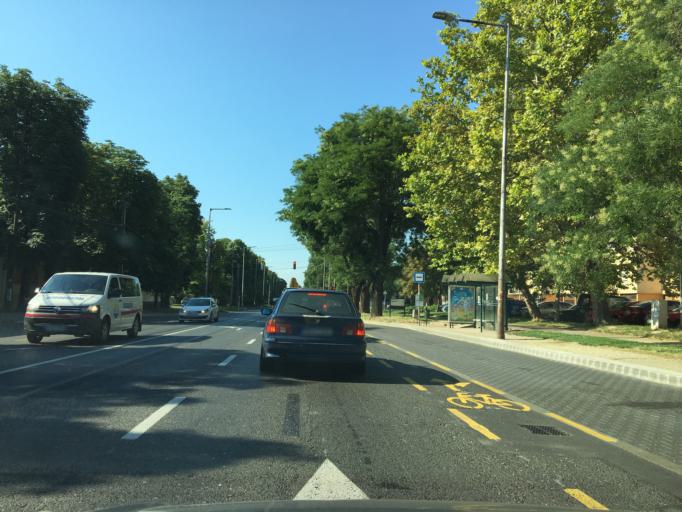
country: HU
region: Tolna
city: Szekszard
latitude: 46.3597
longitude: 18.7041
